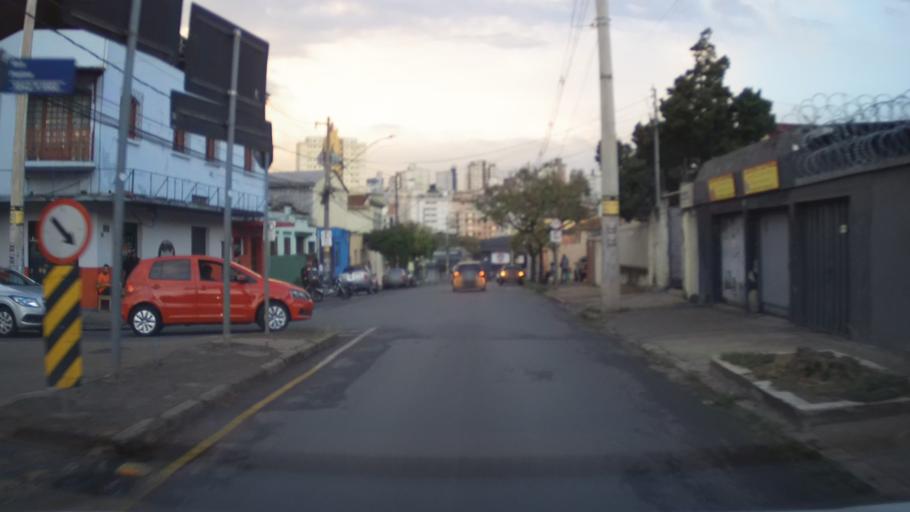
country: BR
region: Minas Gerais
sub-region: Belo Horizonte
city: Belo Horizonte
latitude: -19.9277
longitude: -43.9742
